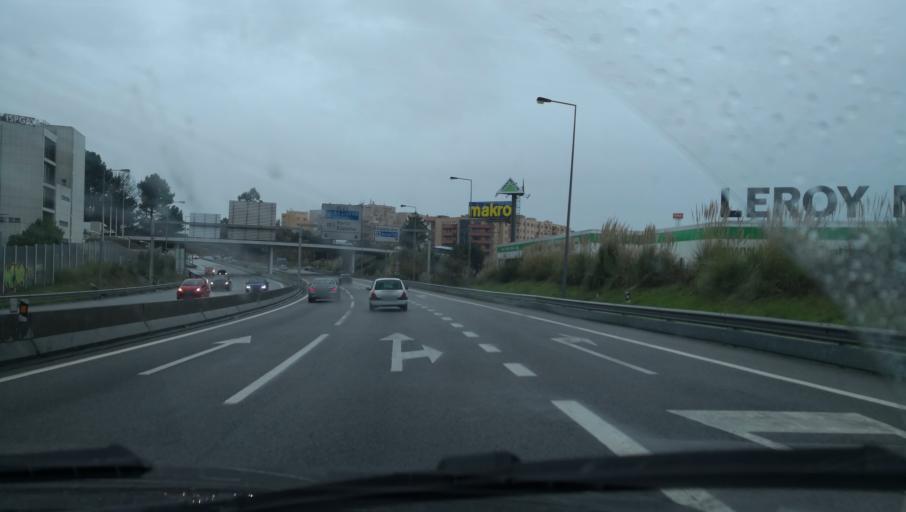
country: PT
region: Porto
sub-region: Vila Nova de Gaia
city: Vila Nova de Gaia
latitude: 41.1210
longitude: -8.6229
